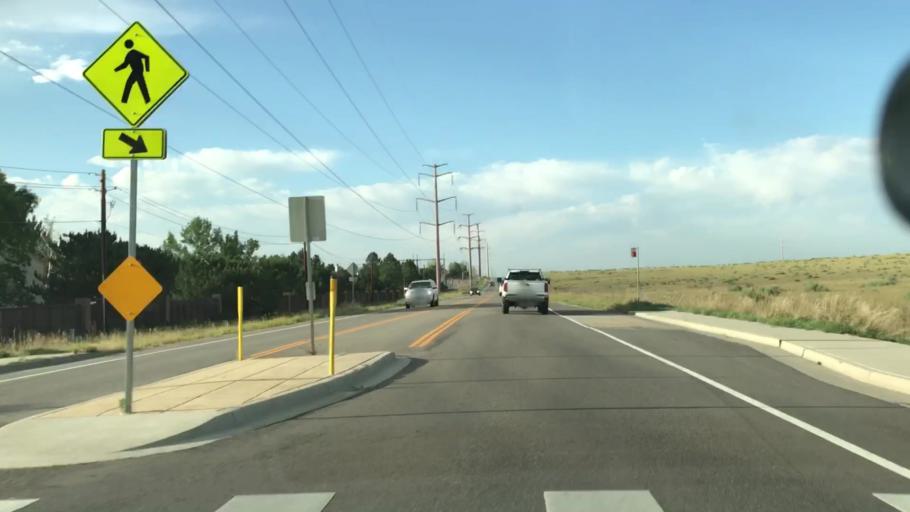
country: US
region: Colorado
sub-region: Boulder County
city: Gunbarrel
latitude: 40.0657
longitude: -105.1785
